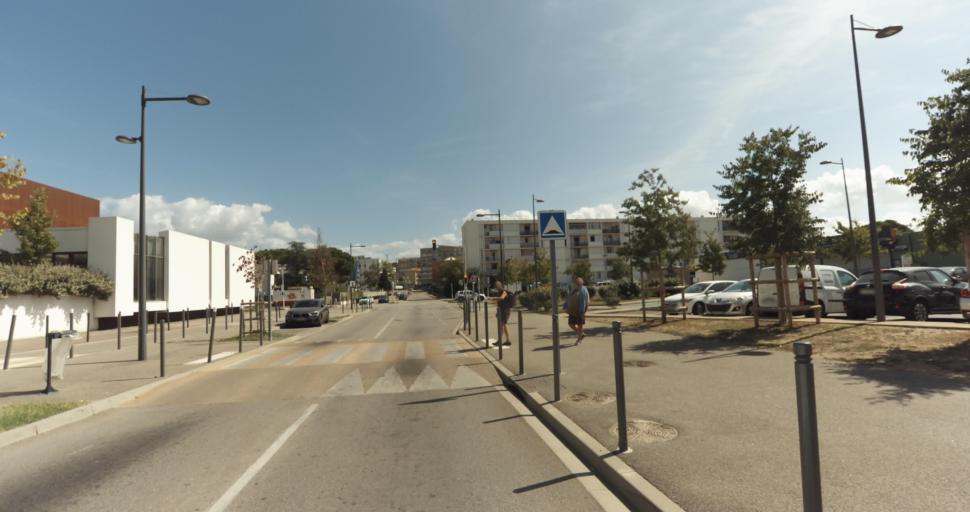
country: FR
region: Corsica
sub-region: Departement de la Corse-du-Sud
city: Ajaccio
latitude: 41.9351
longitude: 8.7500
